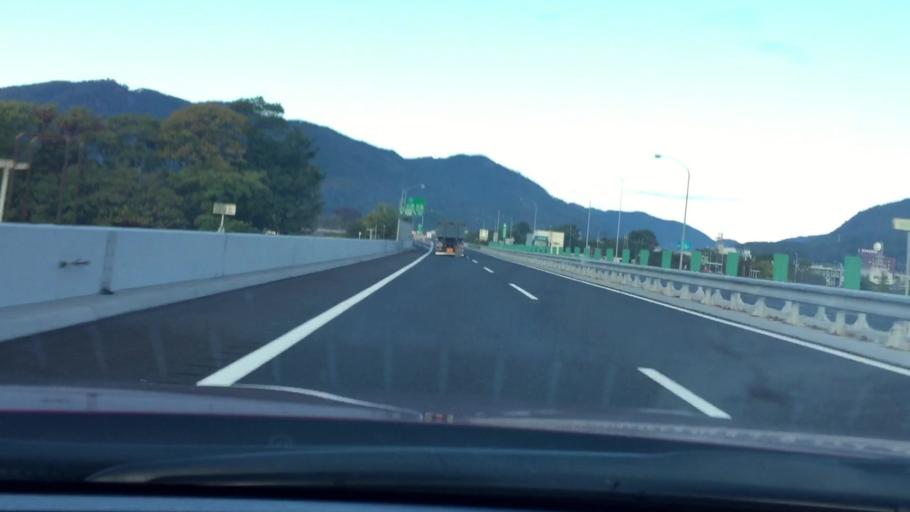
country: JP
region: Hyogo
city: Yamazakicho-nakabirose
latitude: 34.9983
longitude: 134.5531
